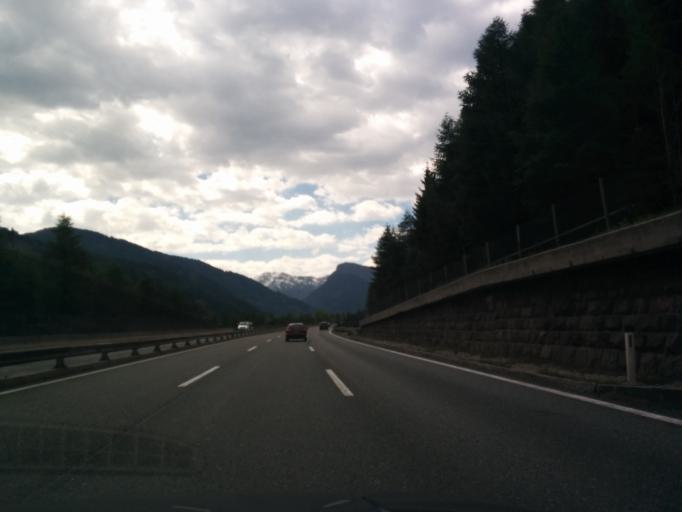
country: AT
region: Tyrol
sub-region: Politischer Bezirk Innsbruck Land
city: Steinach am Brenner
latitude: 47.1005
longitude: 11.4601
